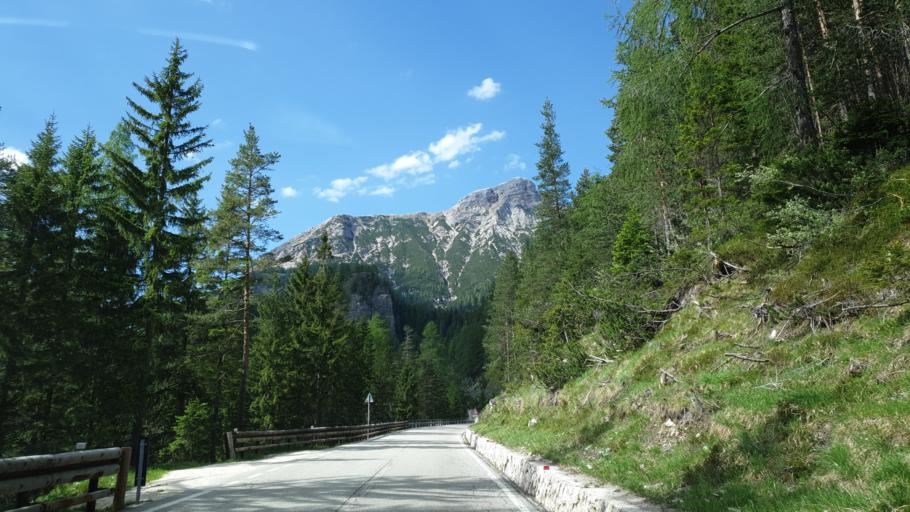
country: IT
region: Veneto
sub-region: Provincia di Belluno
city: Cortina d'Ampezzo
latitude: 46.5902
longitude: 12.1141
